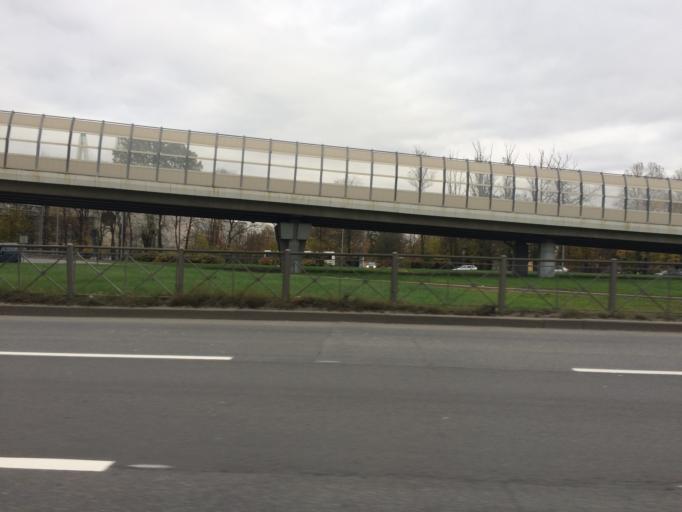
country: RU
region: Leningrad
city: Rybatskoye
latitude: 59.8510
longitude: 30.4804
